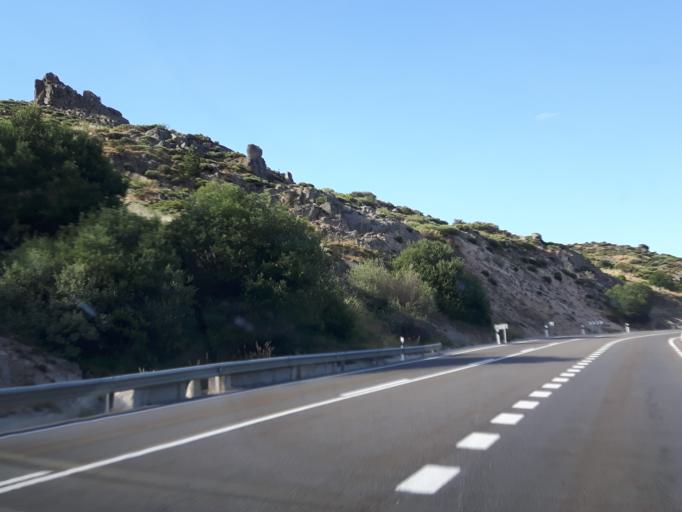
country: ES
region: Castille and Leon
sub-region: Provincia de Avila
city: Mengamunoz
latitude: 40.4806
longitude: -5.0080
